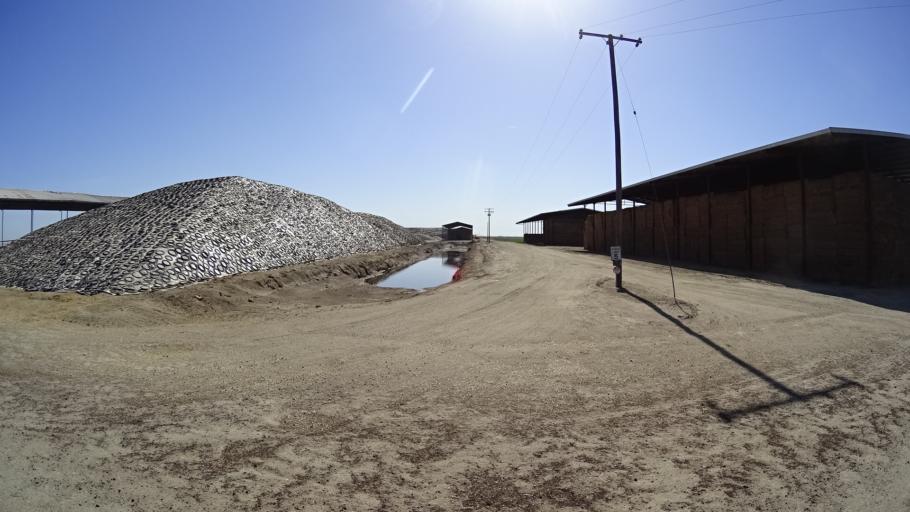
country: US
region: California
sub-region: Kings County
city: Home Garden
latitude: 36.2405
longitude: -119.5562
